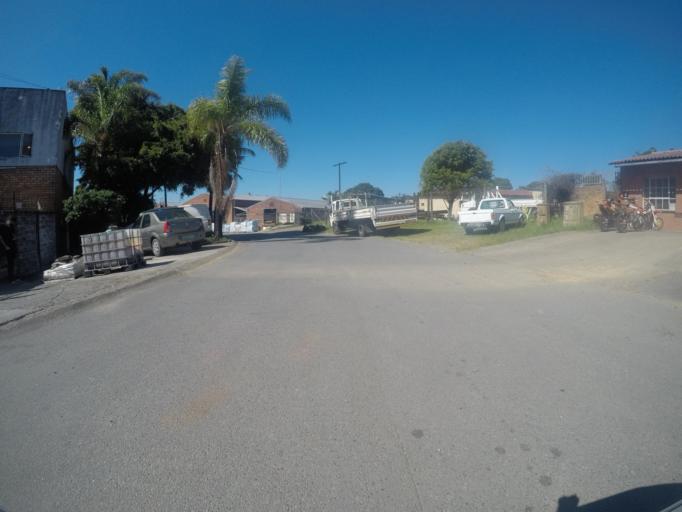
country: ZA
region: Eastern Cape
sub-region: Buffalo City Metropolitan Municipality
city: East London
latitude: -32.9394
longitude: 28.0018
